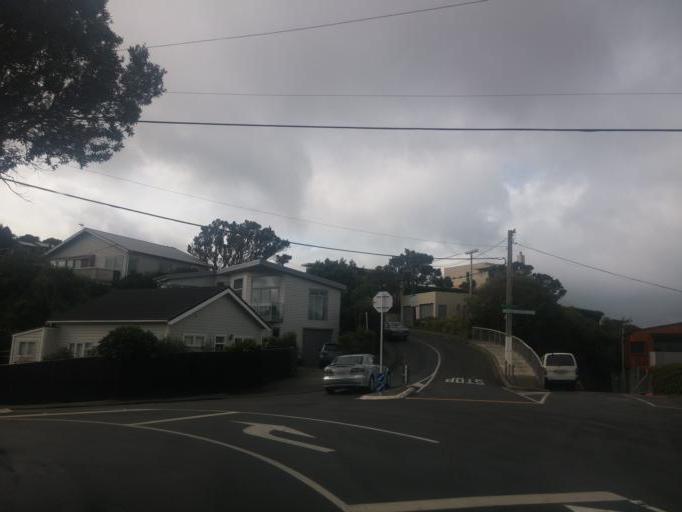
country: NZ
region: Wellington
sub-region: Wellington City
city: Kelburn
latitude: -41.2795
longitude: 174.7615
